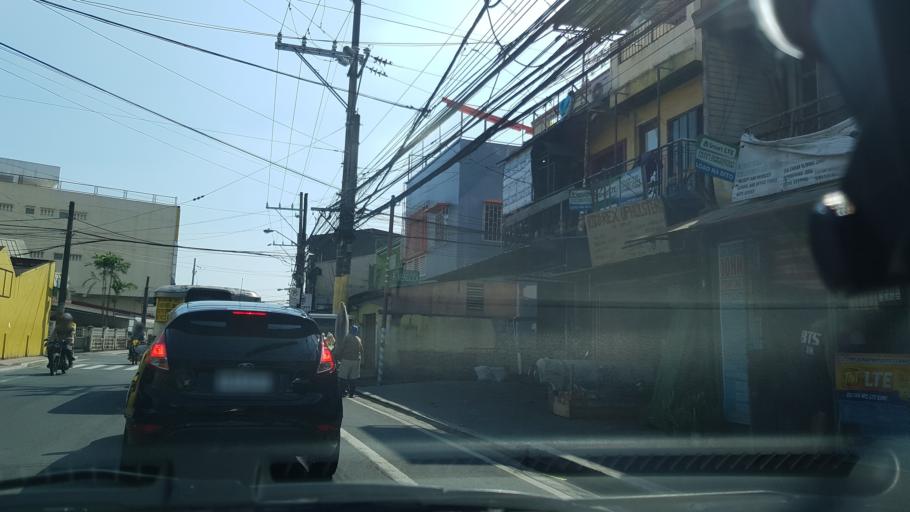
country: PH
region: Metro Manila
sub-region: Marikina
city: Calumpang
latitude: 14.6443
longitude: 121.0958
